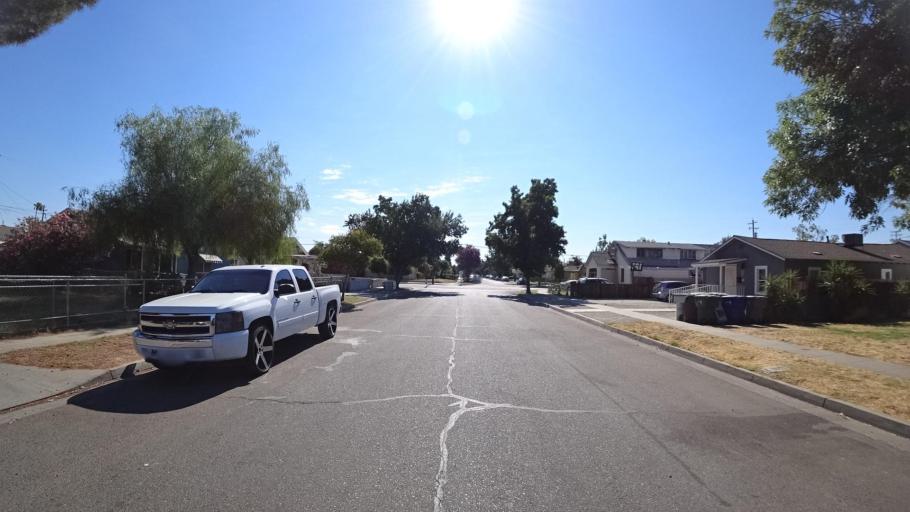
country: US
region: California
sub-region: Fresno County
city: Fresno
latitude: 36.7314
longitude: -119.7586
